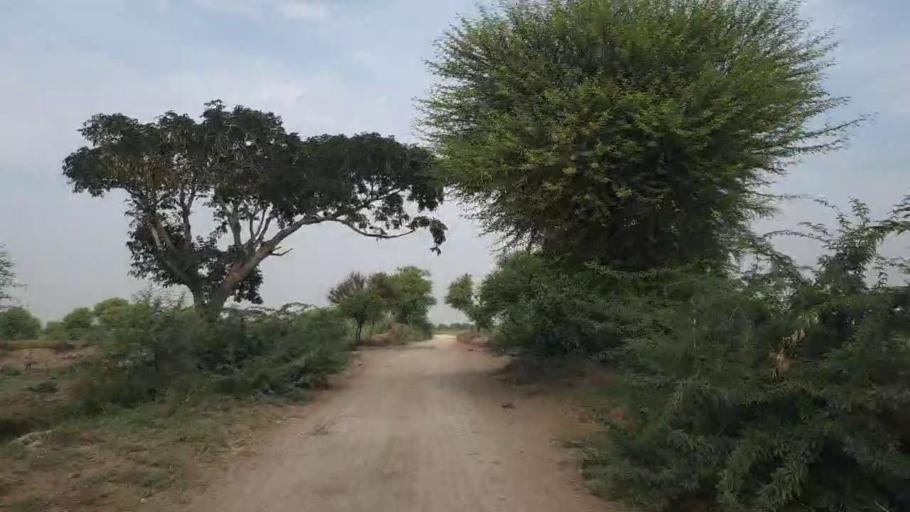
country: PK
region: Sindh
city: Rajo Khanani
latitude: 24.9714
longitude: 68.9962
